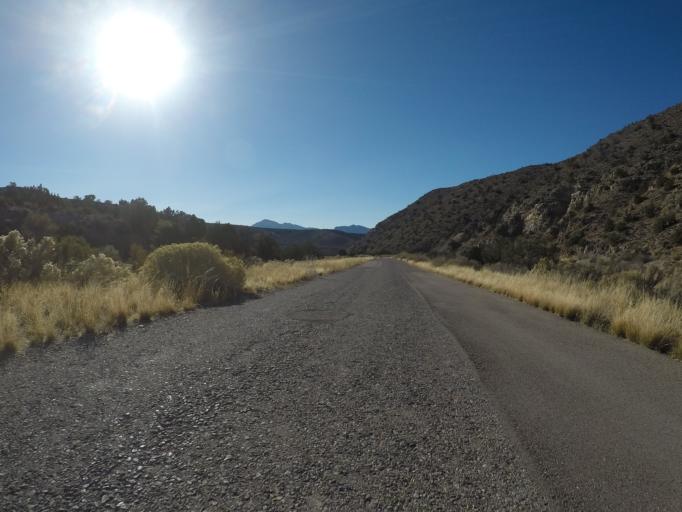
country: US
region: Nevada
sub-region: Clark County
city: Summerlin South
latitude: 36.1009
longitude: -115.5680
